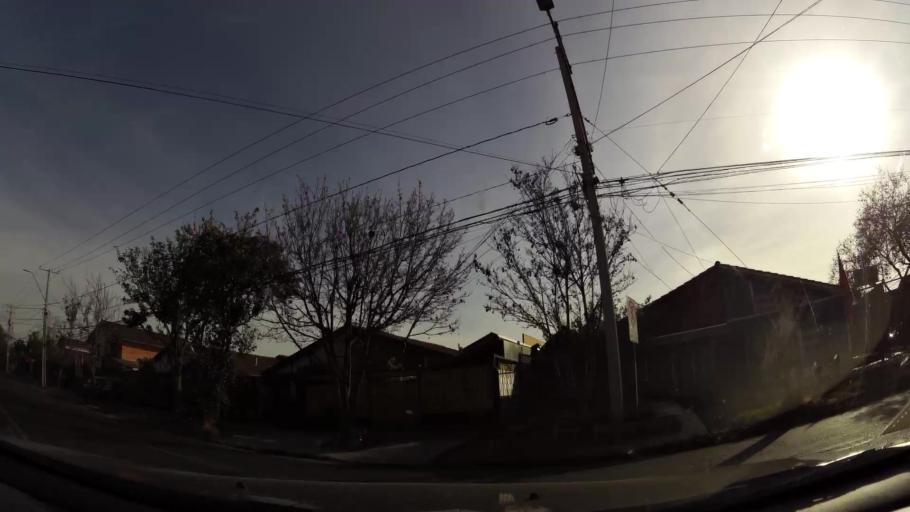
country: CL
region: Santiago Metropolitan
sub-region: Provincia de Cordillera
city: Puente Alto
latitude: -33.5786
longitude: -70.5696
